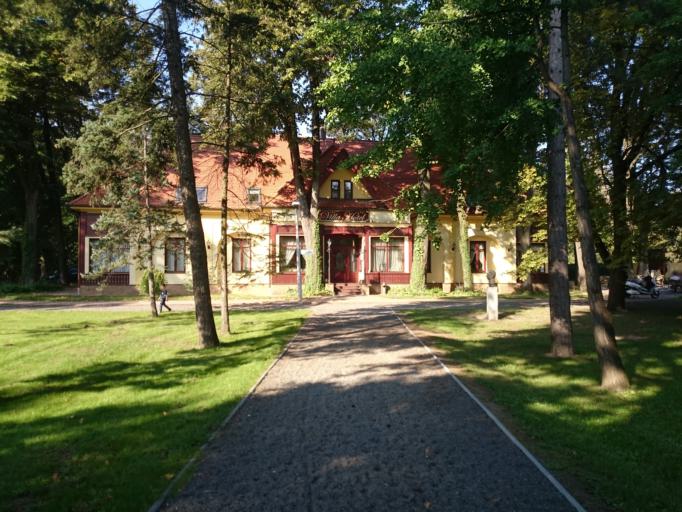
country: HU
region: Hajdu-Bihar
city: Debrecen
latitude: 47.5511
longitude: 21.6289
